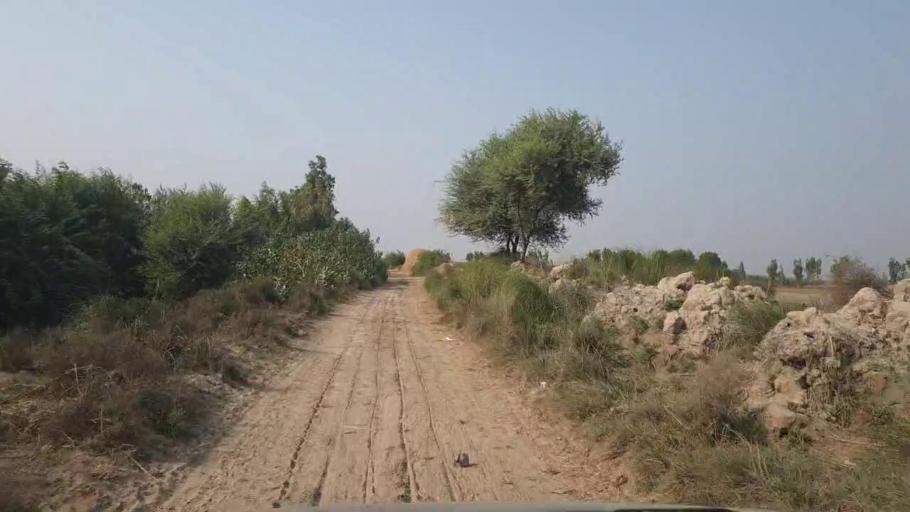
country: PK
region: Sindh
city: Tando Muhammad Khan
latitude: 25.0757
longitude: 68.3537
